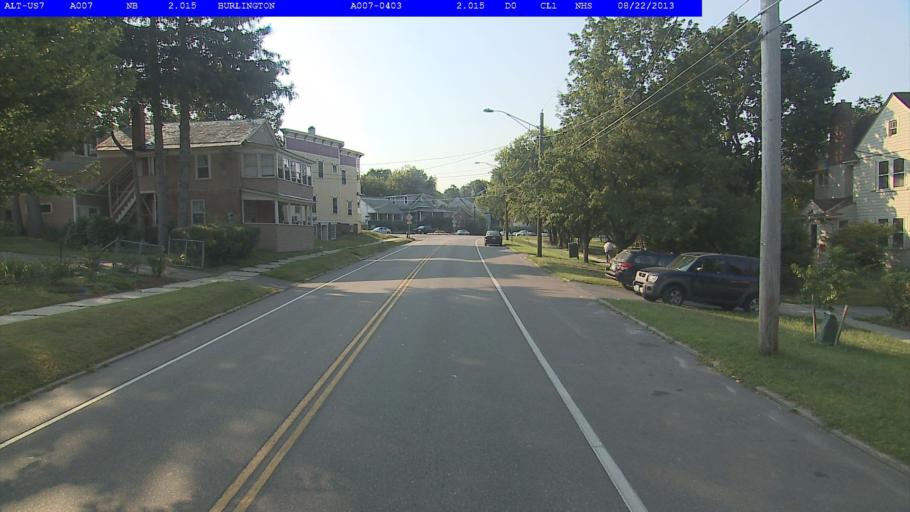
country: US
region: Vermont
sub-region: Chittenden County
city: Burlington
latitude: 44.4658
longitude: -73.2083
